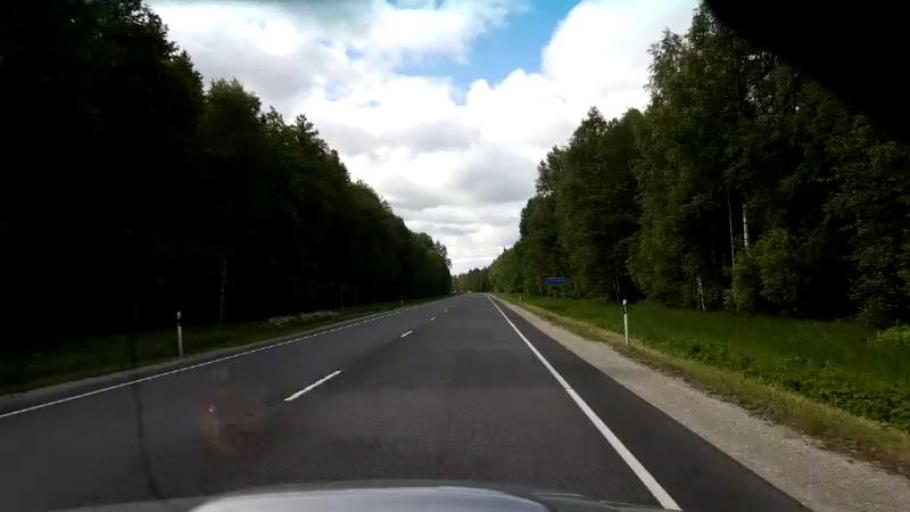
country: EE
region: Raplamaa
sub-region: Maerjamaa vald
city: Marjamaa
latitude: 58.8282
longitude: 24.4164
